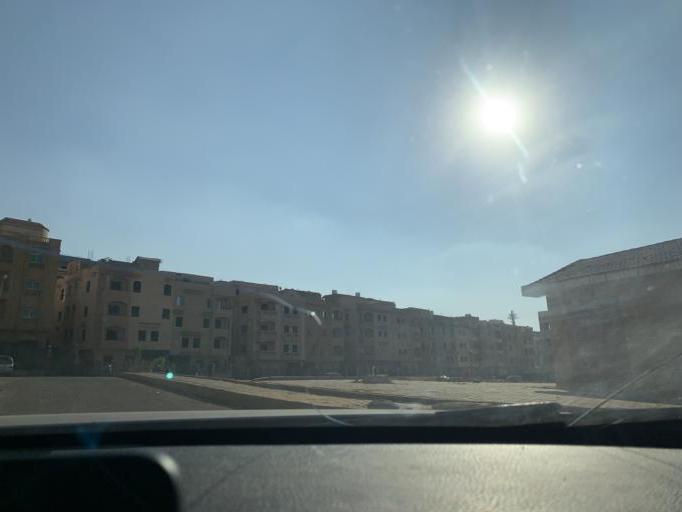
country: EG
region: Muhafazat al Qalyubiyah
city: Al Khankah
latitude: 30.0014
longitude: 31.4833
